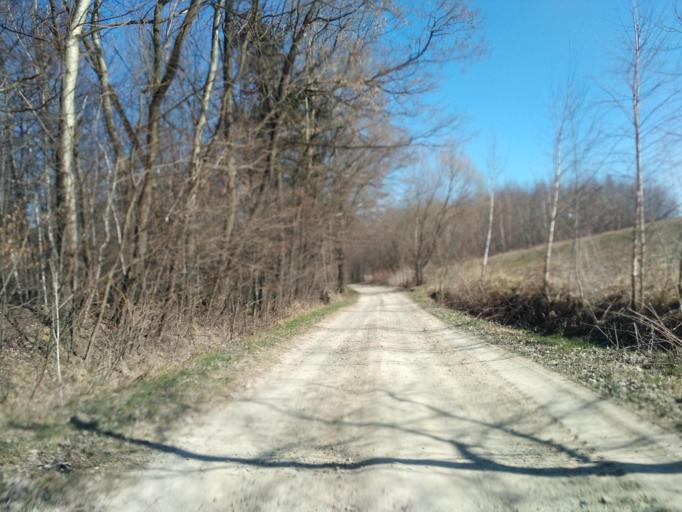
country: PL
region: Subcarpathian Voivodeship
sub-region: Powiat ropczycko-sedziszowski
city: Wielopole Skrzynskie
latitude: 49.9500
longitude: 21.5766
